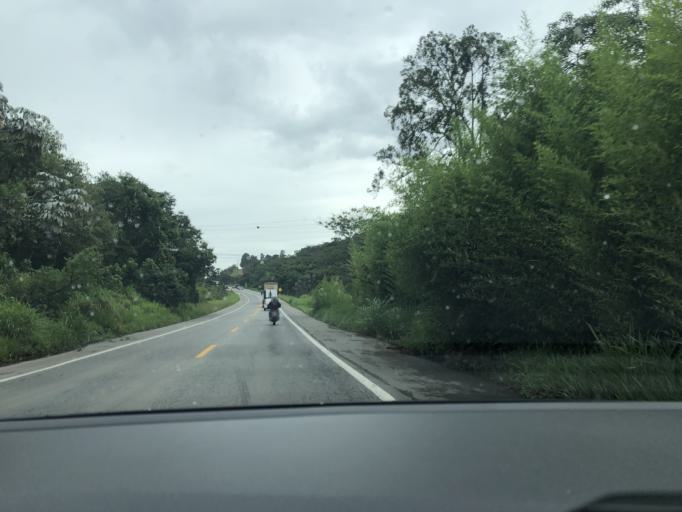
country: BR
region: Sao Paulo
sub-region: Jarinu
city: Jarinu
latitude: -23.1376
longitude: -46.7408
